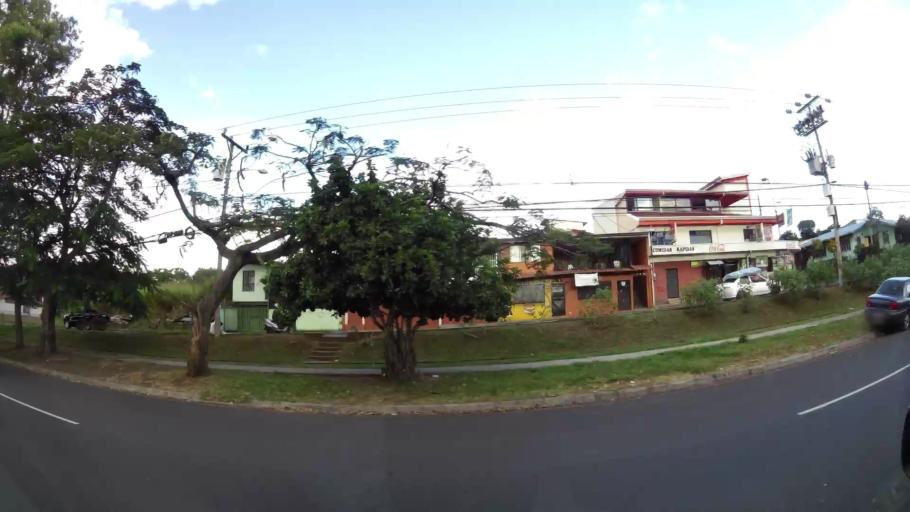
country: CR
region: Alajuela
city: Alajuela
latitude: 10.0070
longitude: -84.2065
